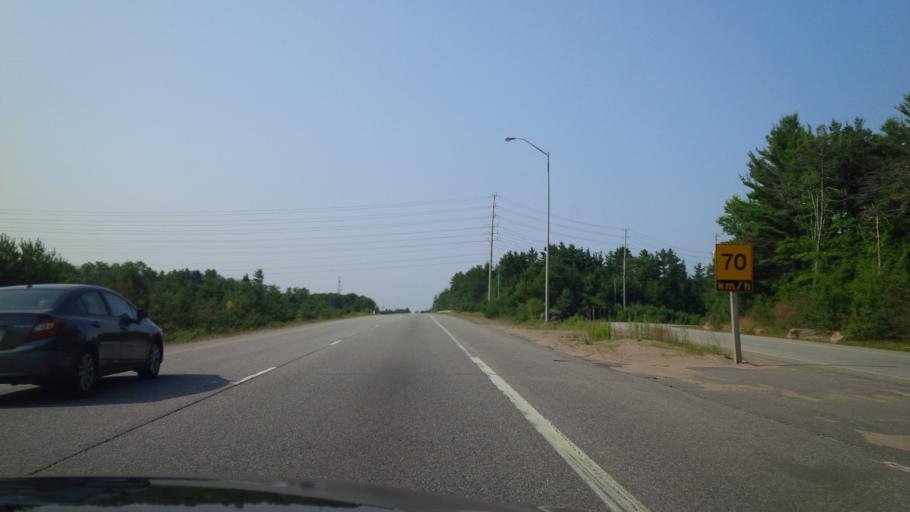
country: CA
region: Ontario
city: Huntsville
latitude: 45.2172
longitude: -79.3139
